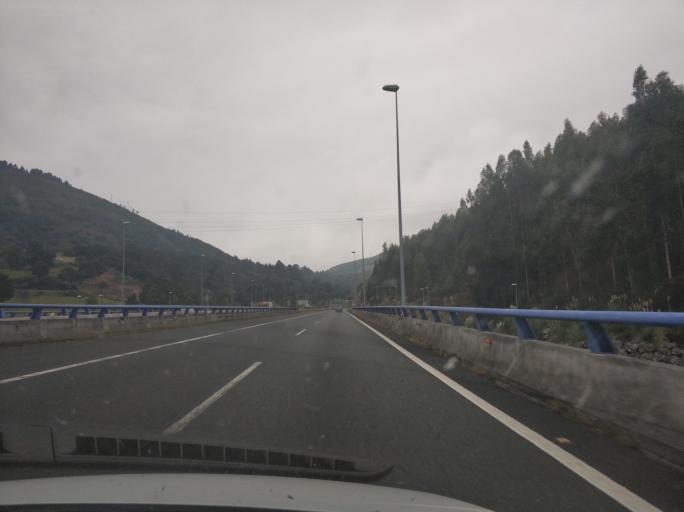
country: ES
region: Cantabria
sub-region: Provincia de Cantabria
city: Los Corrales de Buelna
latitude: 43.2521
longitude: -4.0742
